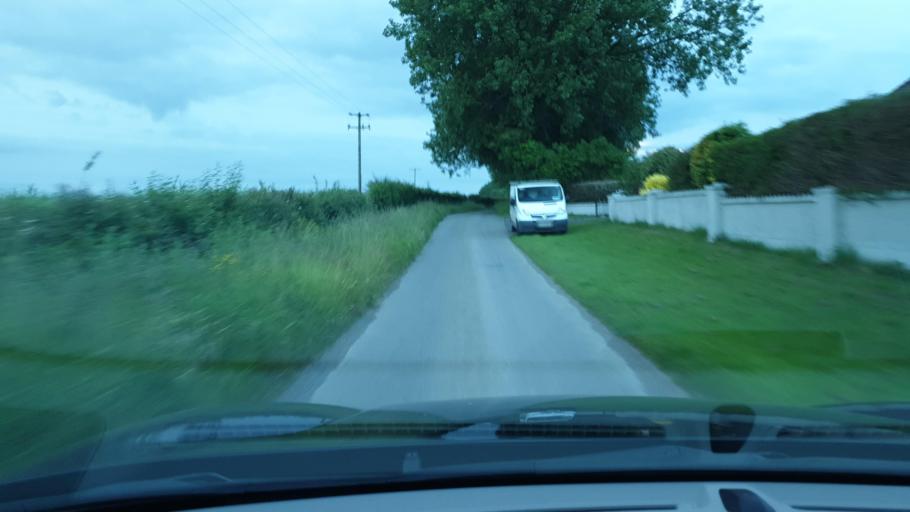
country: IE
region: Leinster
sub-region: An Mhi
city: Ashbourne
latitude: 53.5434
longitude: -6.3498
